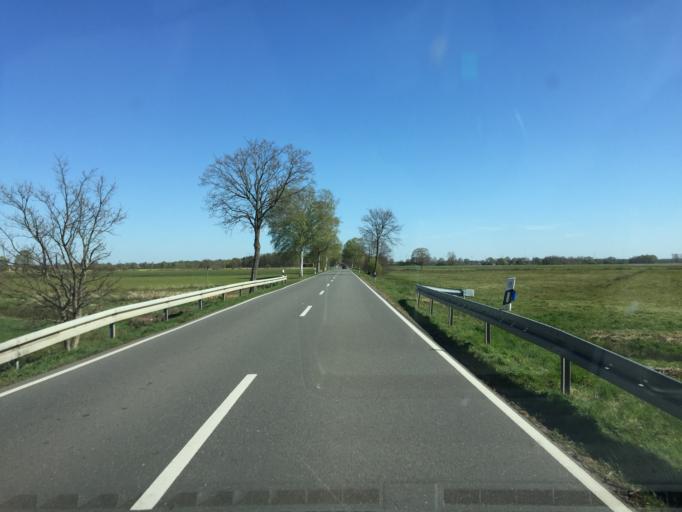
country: DE
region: Lower Saxony
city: Wehrbleck
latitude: 52.5731
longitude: 8.6921
